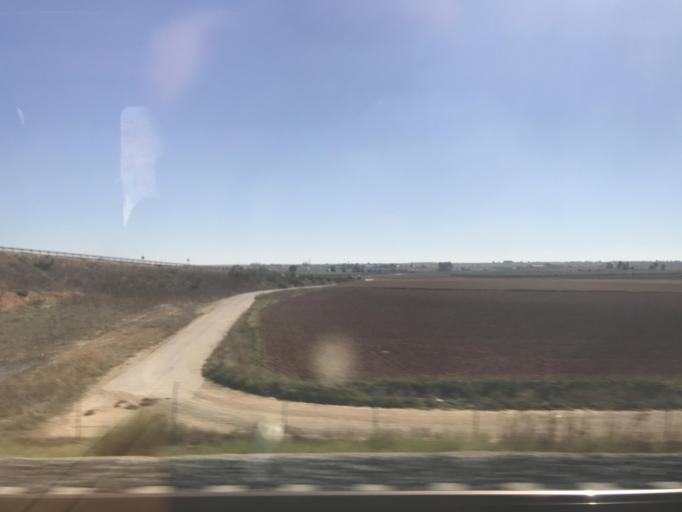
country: ES
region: Castille-La Mancha
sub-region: Province of Toledo
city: Santa Cruz de la Zarza
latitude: 39.9703
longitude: -3.1741
